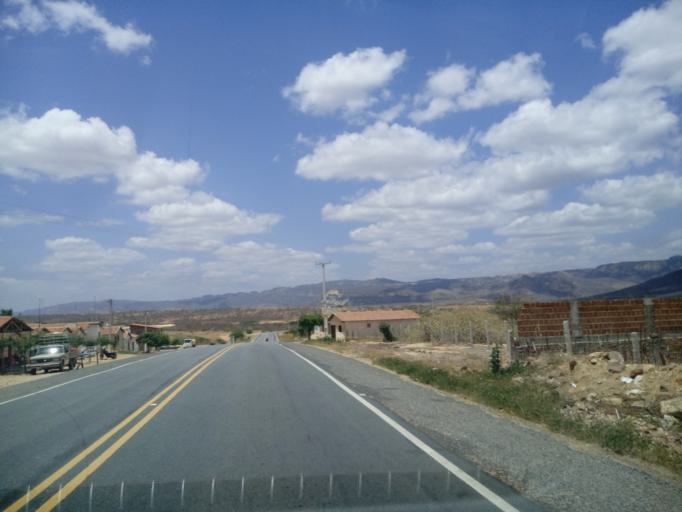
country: BR
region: Paraiba
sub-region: Desterro
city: Desterro
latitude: -7.1198
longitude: -37.0644
